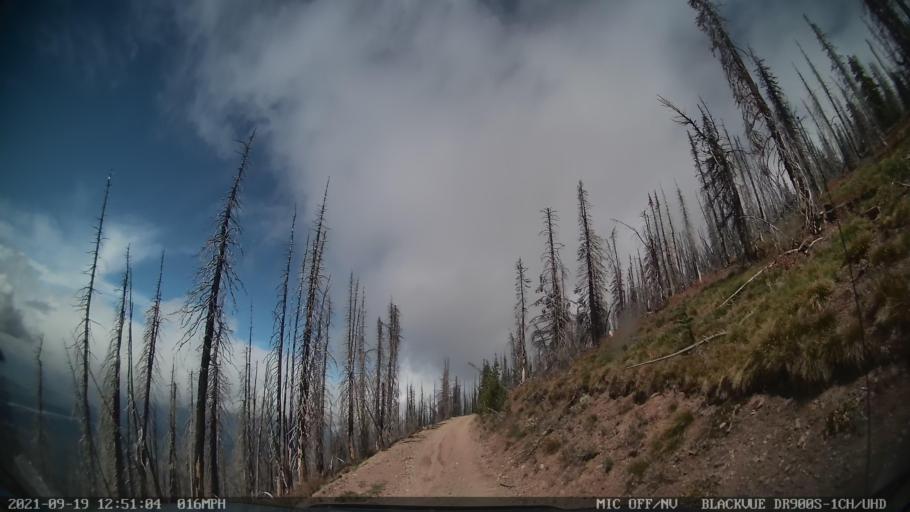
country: US
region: Montana
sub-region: Missoula County
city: Seeley Lake
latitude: 47.1879
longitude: -113.3590
